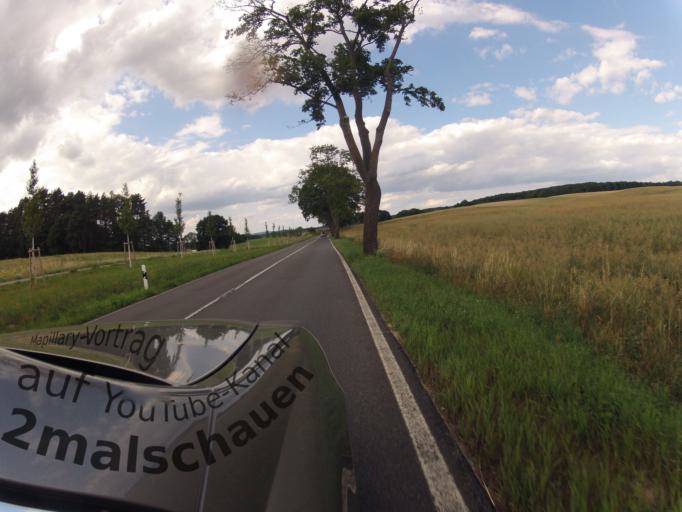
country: DE
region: Mecklenburg-Vorpommern
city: Seebad Heringsdorf
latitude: 53.8960
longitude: 14.1448
